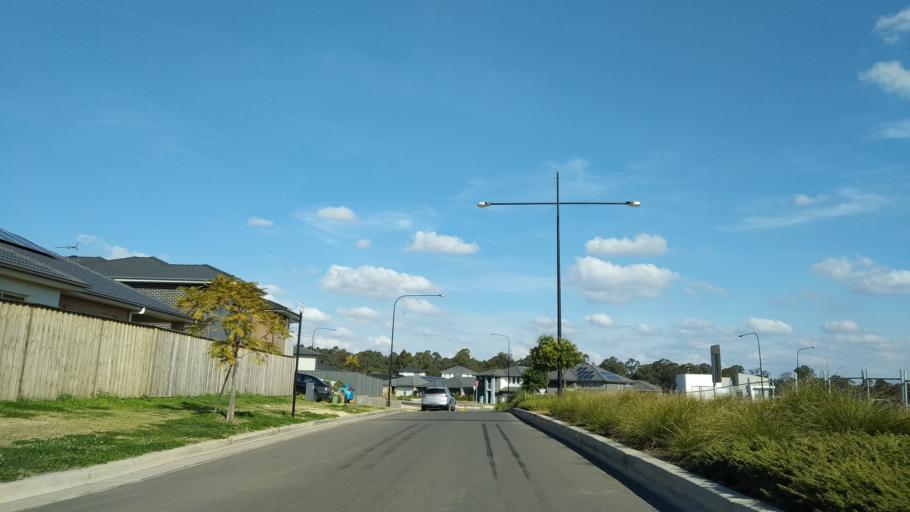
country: AU
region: New South Wales
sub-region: Blacktown
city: Hassall Grove
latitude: -33.7216
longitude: 150.8533
